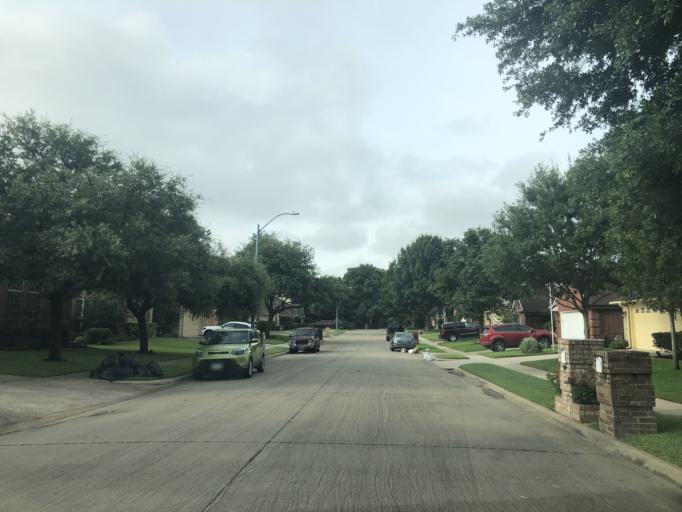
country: US
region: Texas
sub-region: Dallas County
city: Irving
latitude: 32.8026
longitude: -96.9801
